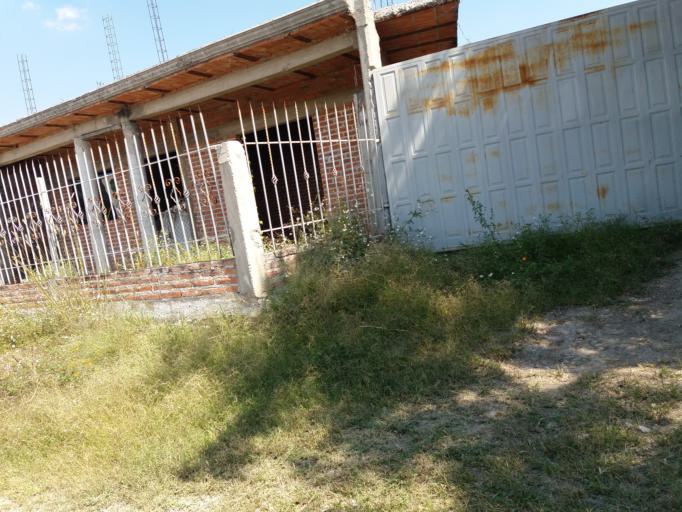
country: MX
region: Aguascalientes
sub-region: Aguascalientes
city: Penuelas (El Cienegal)
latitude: 21.7500
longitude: -102.3033
